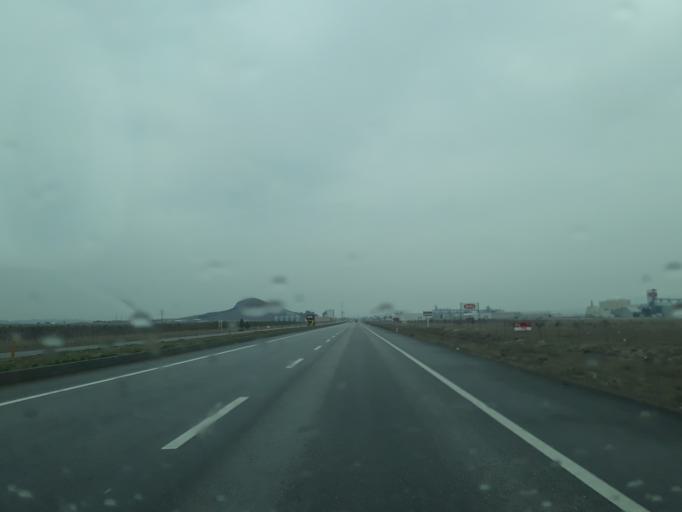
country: TR
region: Konya
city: Karapinar
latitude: 37.7126
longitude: 33.6048
